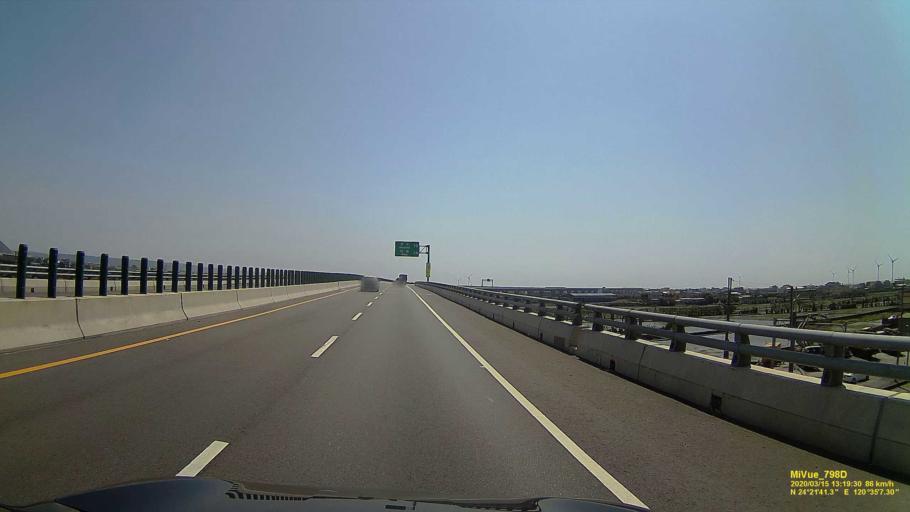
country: TW
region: Taiwan
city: Fengyuan
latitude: 24.3612
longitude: 120.5853
